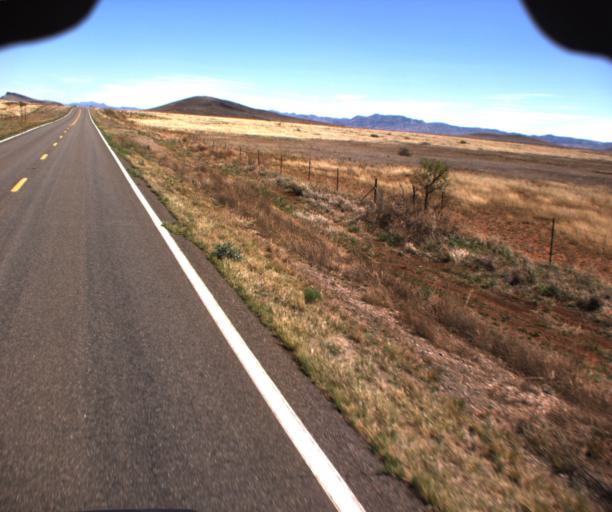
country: US
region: Arizona
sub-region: Cochise County
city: Douglas
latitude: 31.6069
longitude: -109.2251
